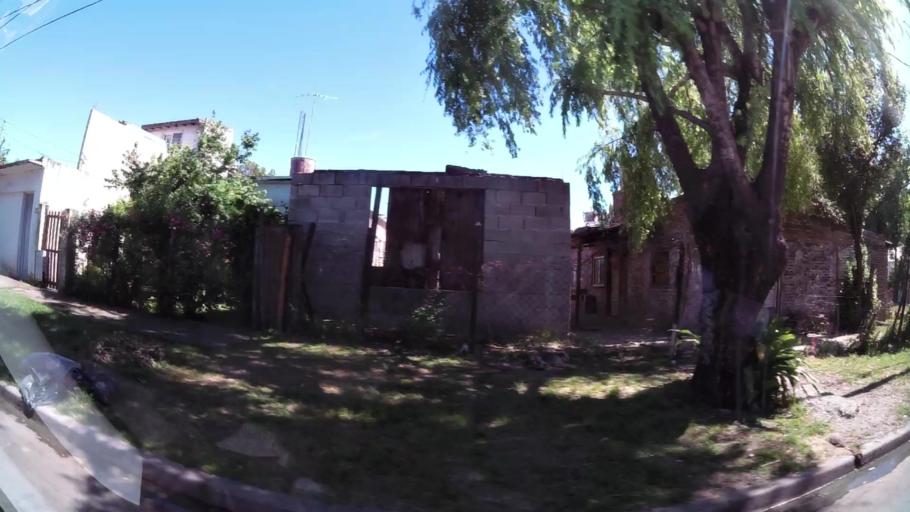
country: AR
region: Buenos Aires
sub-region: Partido de Tigre
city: Tigre
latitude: -34.4987
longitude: -58.6092
